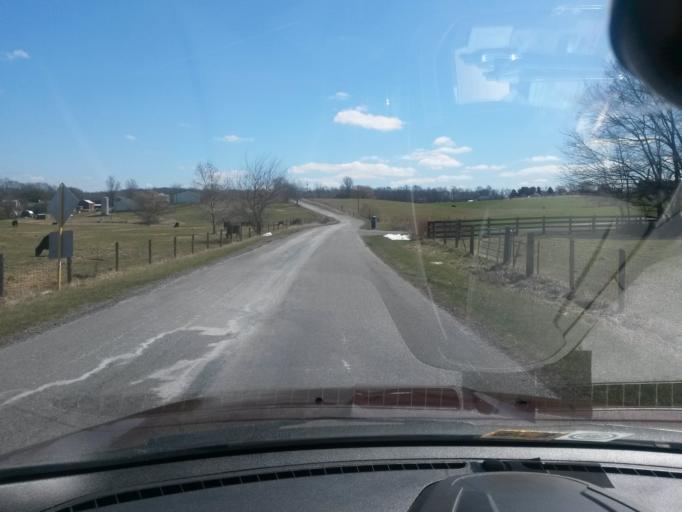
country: US
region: Virginia
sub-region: Augusta County
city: Stuarts Draft
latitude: 38.0441
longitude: -79.0420
